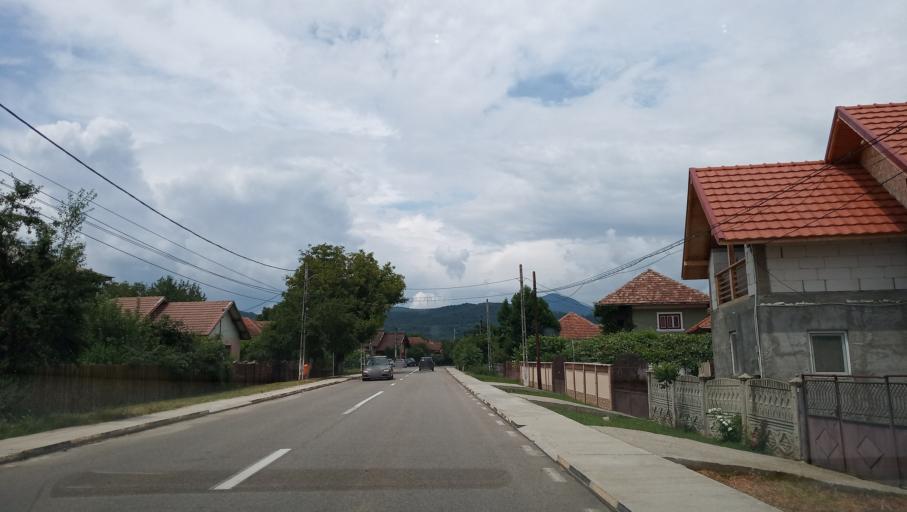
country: RO
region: Gorj
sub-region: Comuna Tismana
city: Tismana
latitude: 45.0455
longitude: 22.9495
